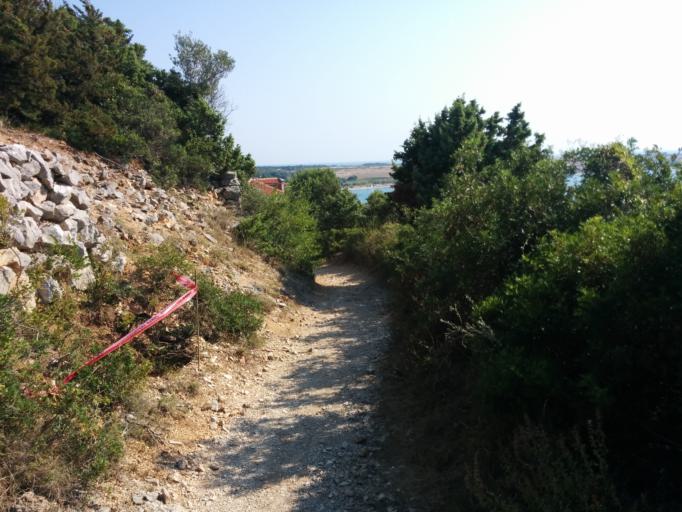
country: HR
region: Primorsko-Goranska
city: Mali Losinj
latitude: 44.6396
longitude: 14.2466
